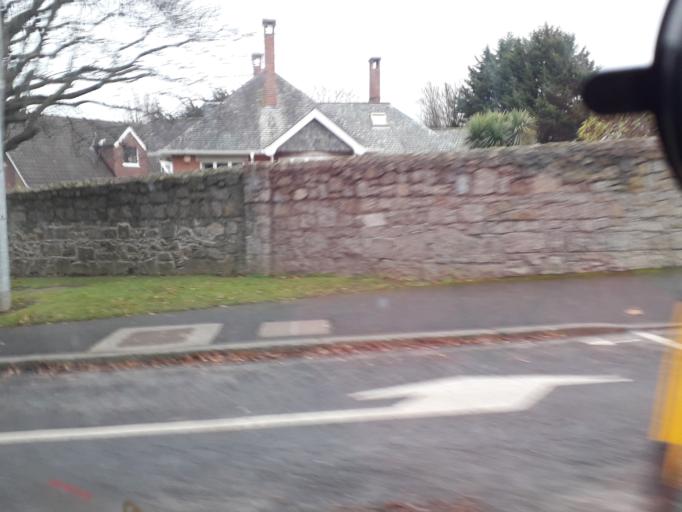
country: IE
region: Leinster
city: Mount Merrion
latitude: 53.3016
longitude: -6.2136
